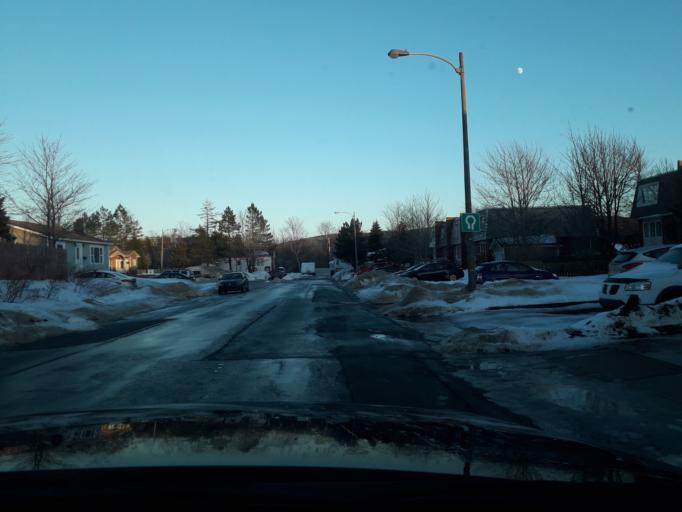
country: CA
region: Newfoundland and Labrador
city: Mount Pearl
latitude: 47.5246
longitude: -52.7637
